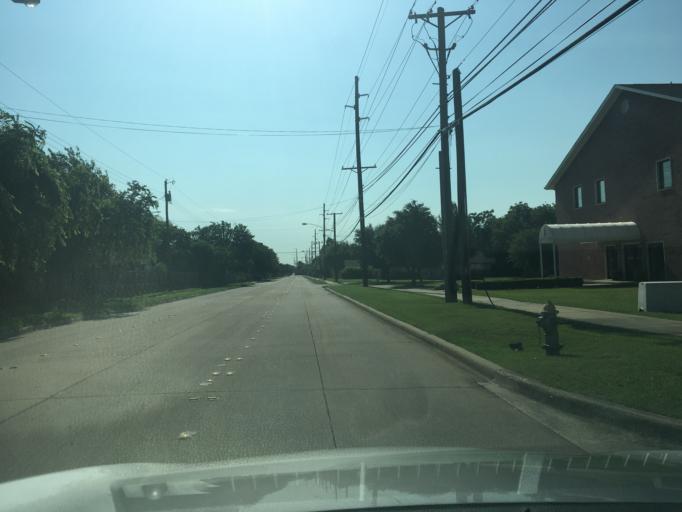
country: US
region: Texas
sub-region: Dallas County
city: Richardson
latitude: 32.9239
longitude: -96.6897
